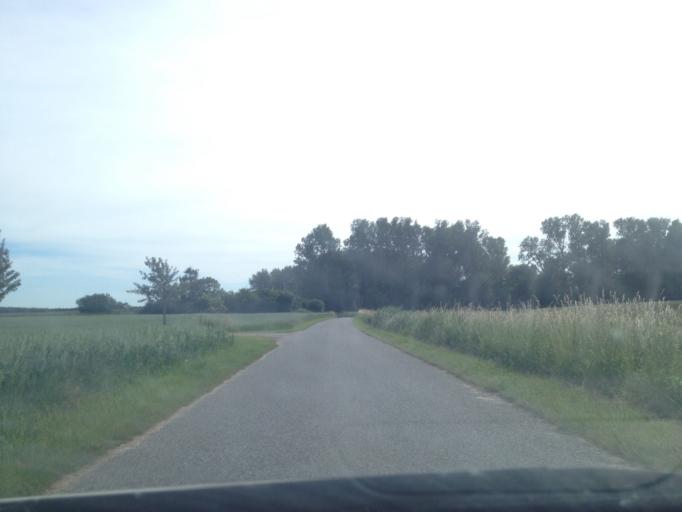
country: DK
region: Central Jutland
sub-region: Samso Kommune
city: Tranebjerg
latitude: 55.7843
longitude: 10.5537
